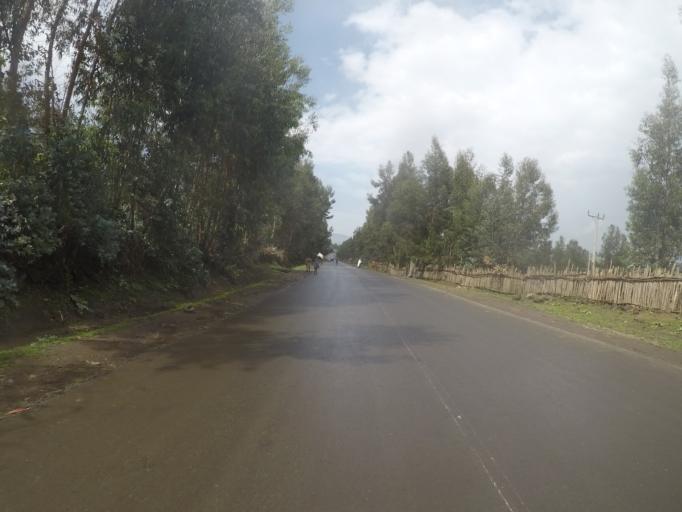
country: ET
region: Amhara
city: Debark'
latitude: 13.1196
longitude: 37.8816
